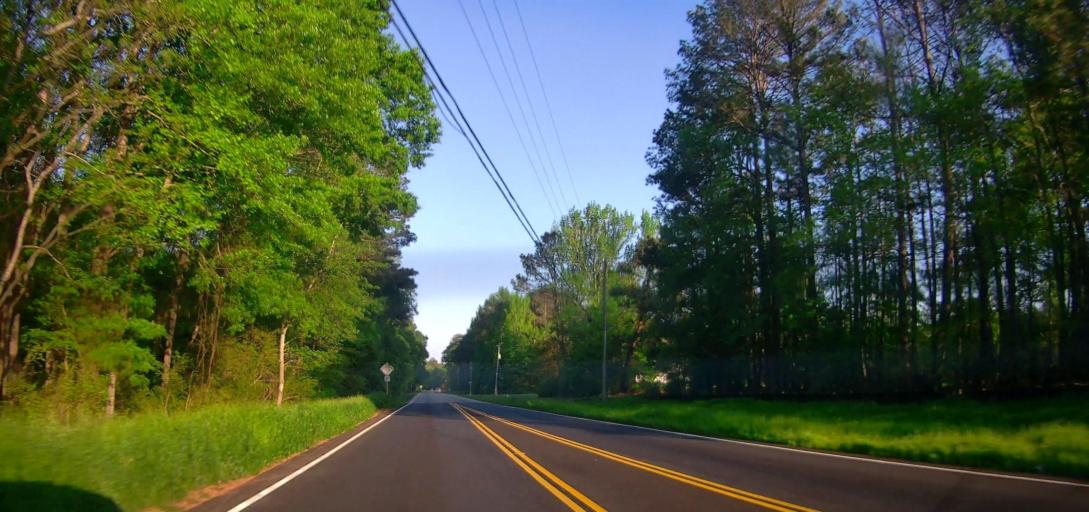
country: US
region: Georgia
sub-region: Newton County
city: Covington
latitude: 33.5898
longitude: -83.7901
